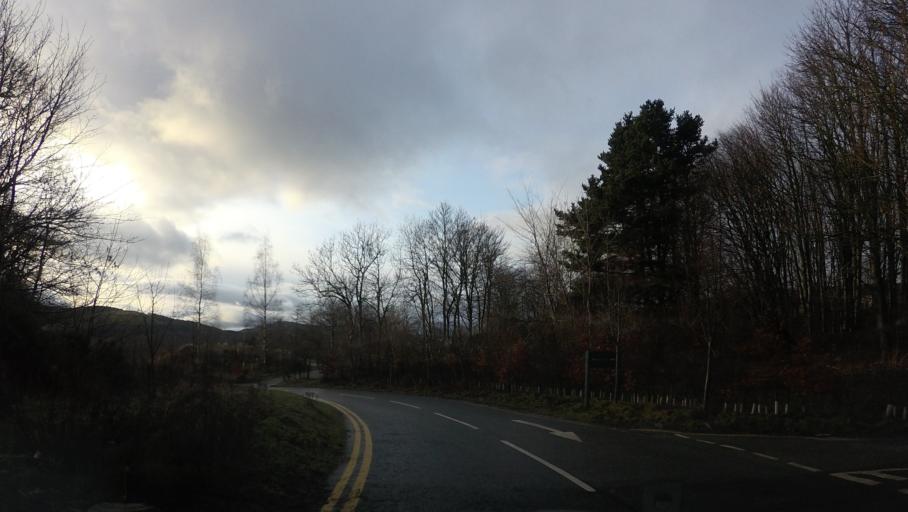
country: GB
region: Scotland
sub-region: The Scottish Borders
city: Peebles
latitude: 55.6465
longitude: -3.1380
